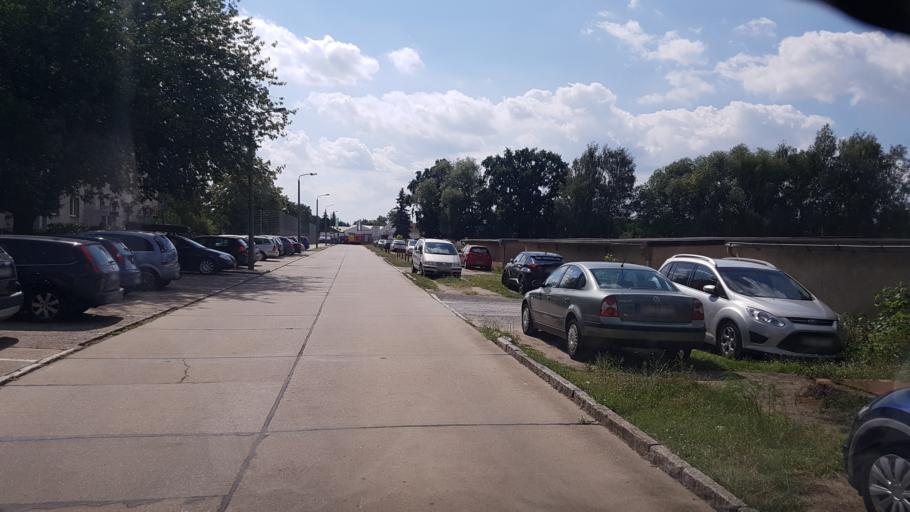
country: DE
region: Brandenburg
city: Lubbenau
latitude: 51.8622
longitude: 13.9371
